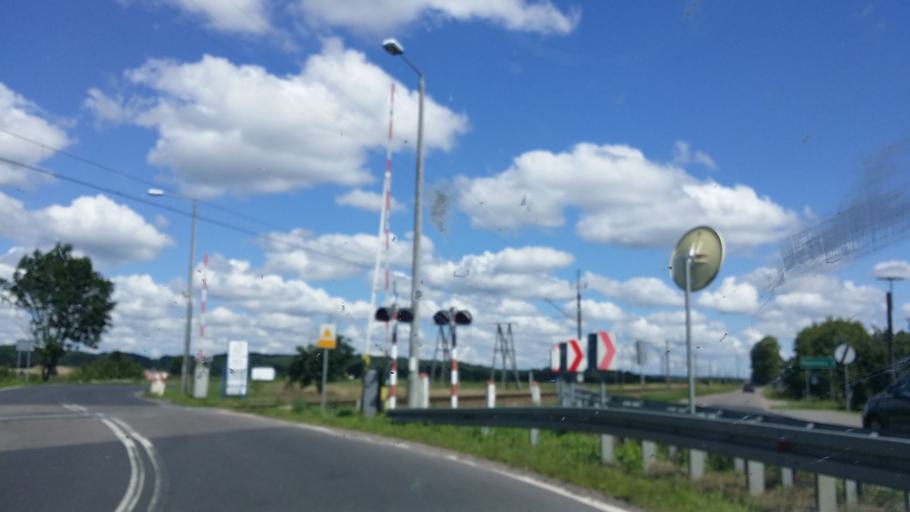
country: PL
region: West Pomeranian Voivodeship
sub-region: Powiat swidwinski
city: Swidwin
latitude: 53.7930
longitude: 15.7810
